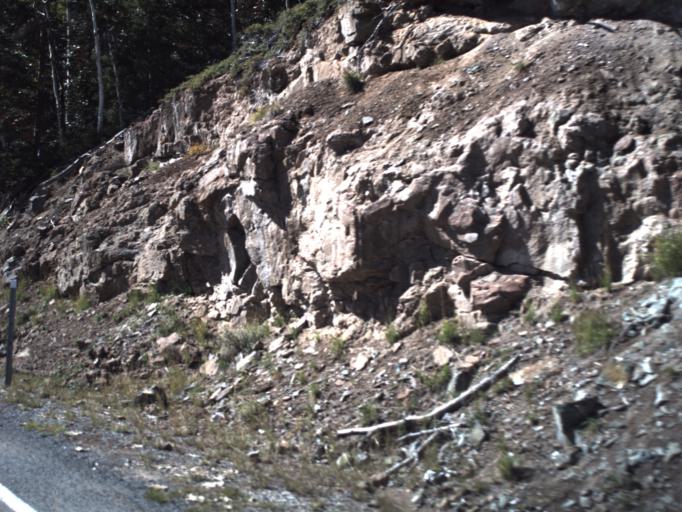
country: US
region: Utah
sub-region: Piute County
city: Junction
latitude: 38.3266
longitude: -112.3729
